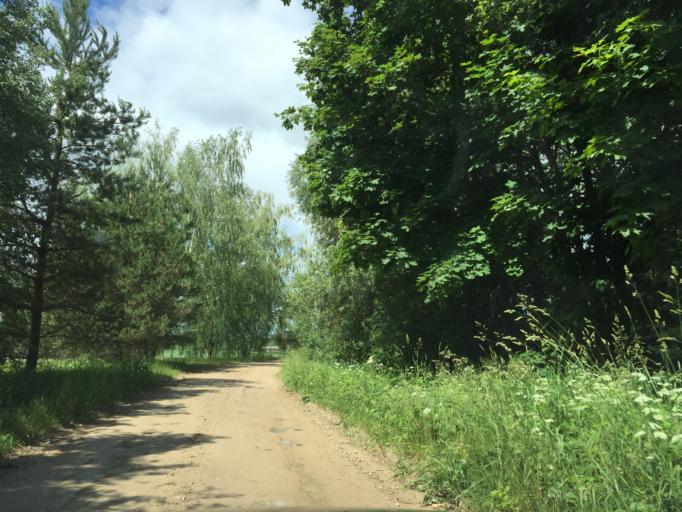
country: LV
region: Lecava
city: Iecava
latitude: 56.5576
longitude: 24.1411
